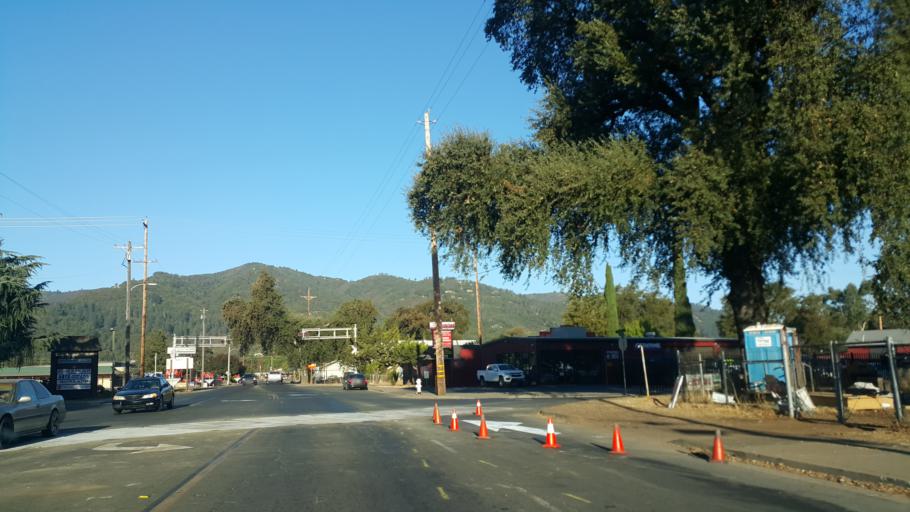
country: US
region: California
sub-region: Mendocino County
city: Ukiah
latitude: 39.1362
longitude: -123.1999
